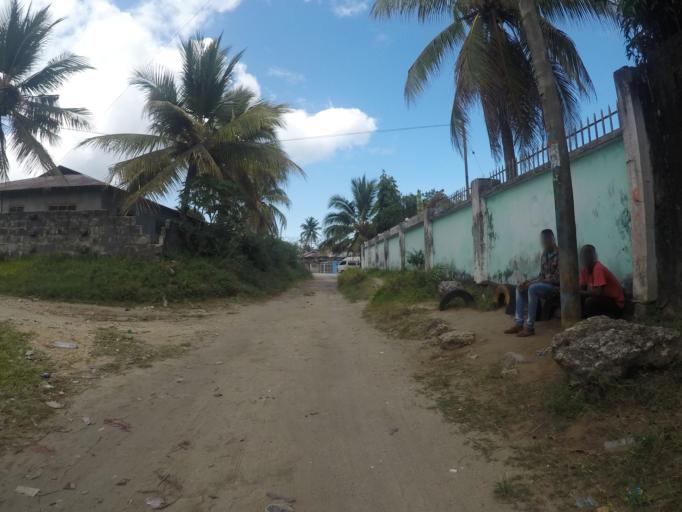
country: TZ
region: Zanzibar Urban/West
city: Zanzibar
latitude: -6.1840
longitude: 39.2117
